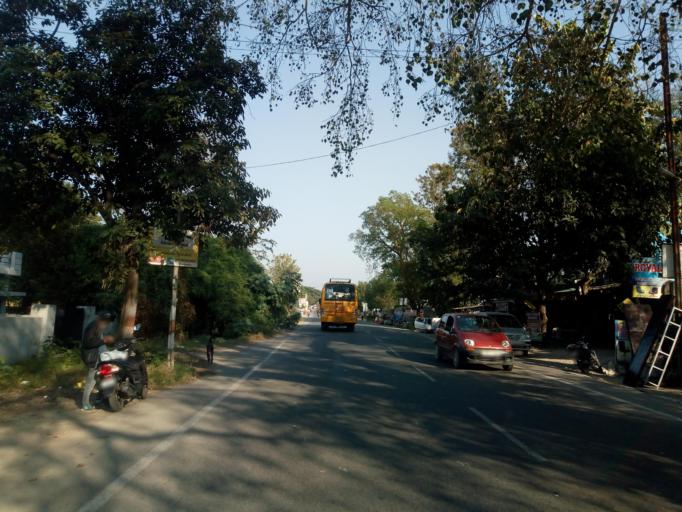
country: IN
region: Uttarakhand
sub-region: Dehradun
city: Dehradun
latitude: 30.3443
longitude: 77.9168
